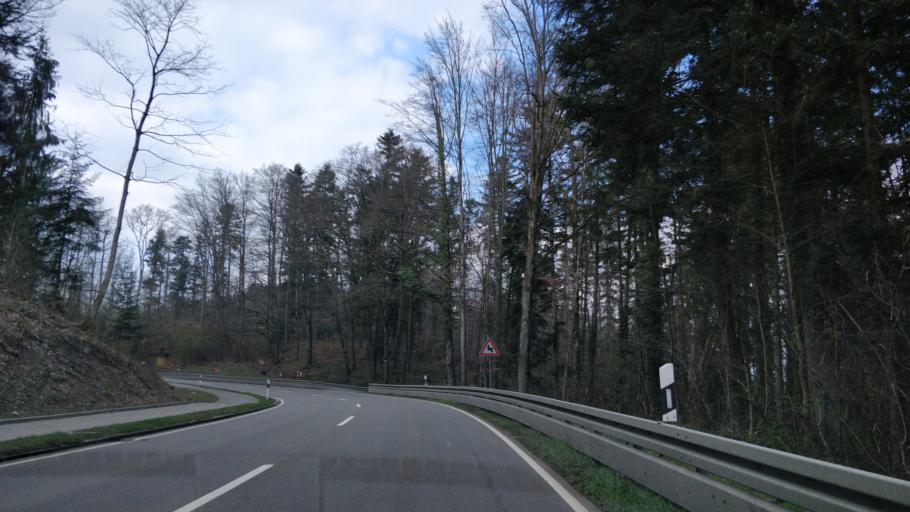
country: DE
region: Baden-Wuerttemberg
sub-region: Regierungsbezirk Stuttgart
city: Fichtenberg
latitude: 48.9862
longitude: 9.6825
